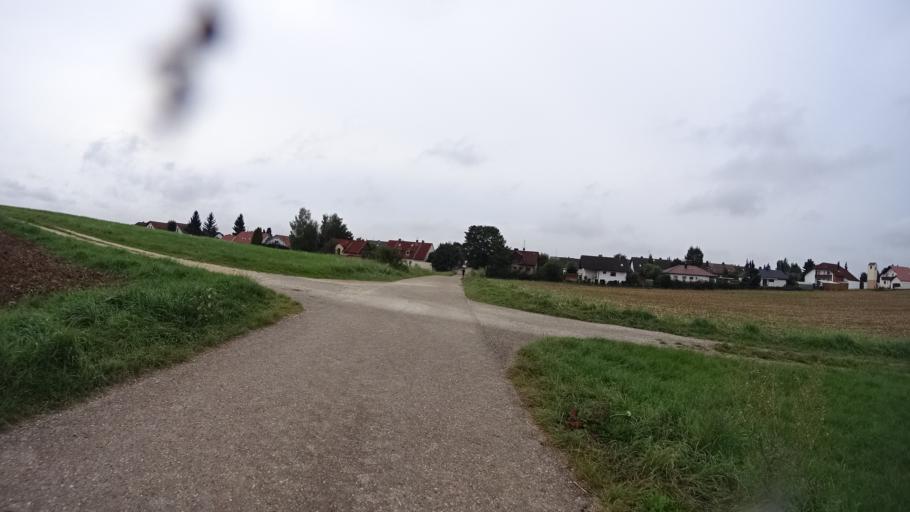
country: DE
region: Bavaria
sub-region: Upper Bavaria
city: Bohmfeld
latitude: 48.8394
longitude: 11.3554
